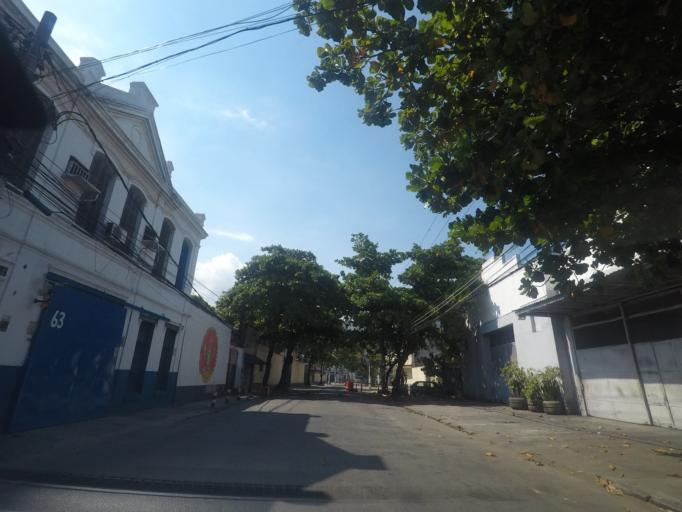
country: BR
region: Rio de Janeiro
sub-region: Rio De Janeiro
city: Rio de Janeiro
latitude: -22.8951
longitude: -43.2180
